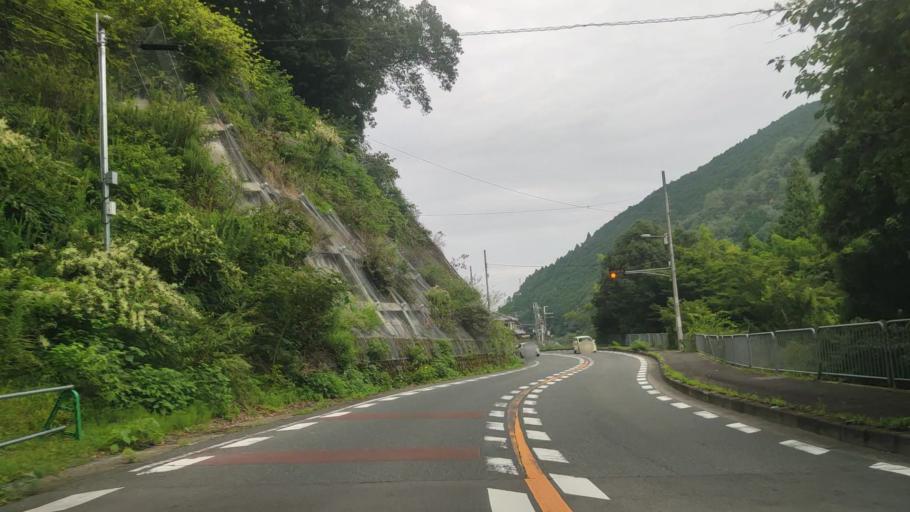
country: JP
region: Wakayama
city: Hashimoto
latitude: 34.3901
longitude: 135.5992
